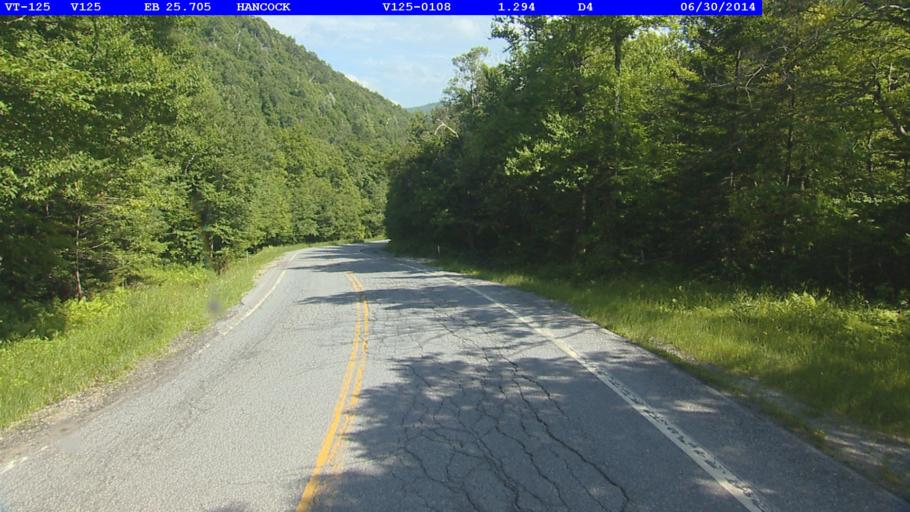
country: US
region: Vermont
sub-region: Rutland County
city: Brandon
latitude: 43.9341
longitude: -72.9484
